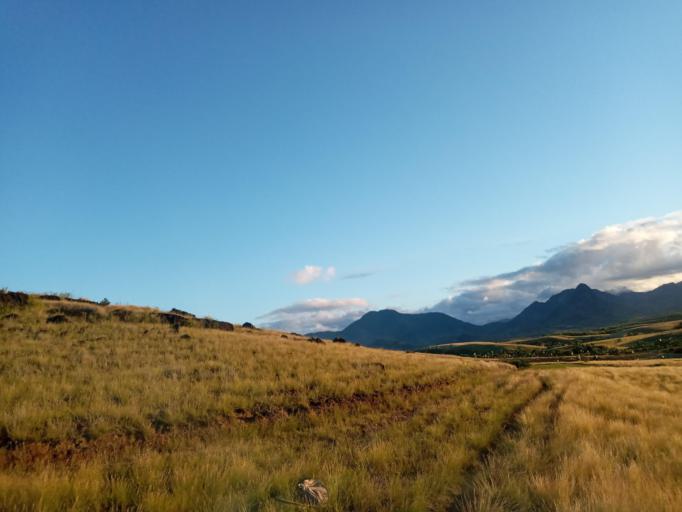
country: MG
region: Anosy
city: Fort Dauphin
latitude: -24.5130
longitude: 47.2518
